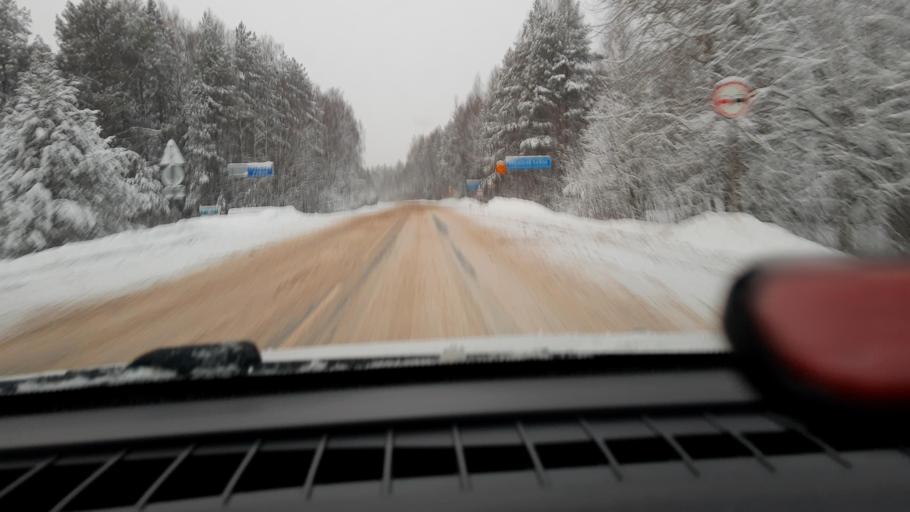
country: RU
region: Nizjnij Novgorod
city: Prudy
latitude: 57.3733
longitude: 46.1625
